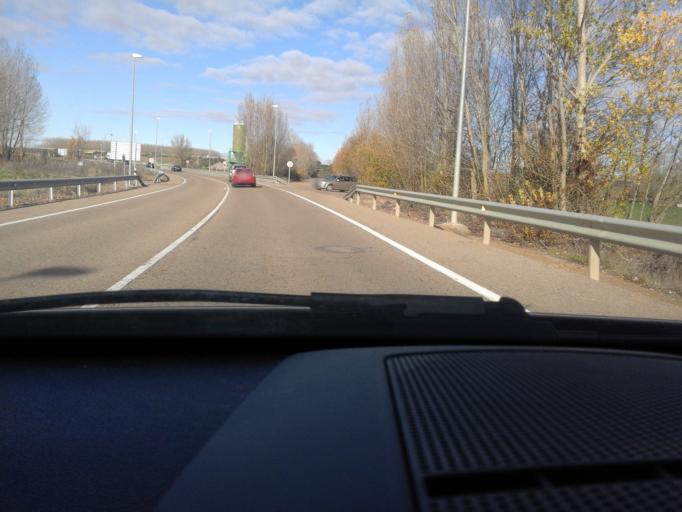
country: ES
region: Castille and Leon
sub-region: Provincia de Palencia
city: Carrion de los Condes
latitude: 42.3466
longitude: -4.6190
